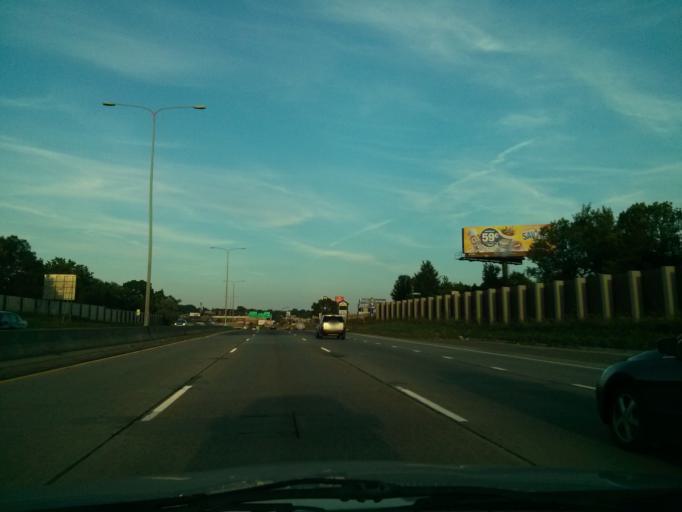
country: US
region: Minnesota
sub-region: Ramsey County
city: Maplewood
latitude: 44.9517
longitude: -93.0313
